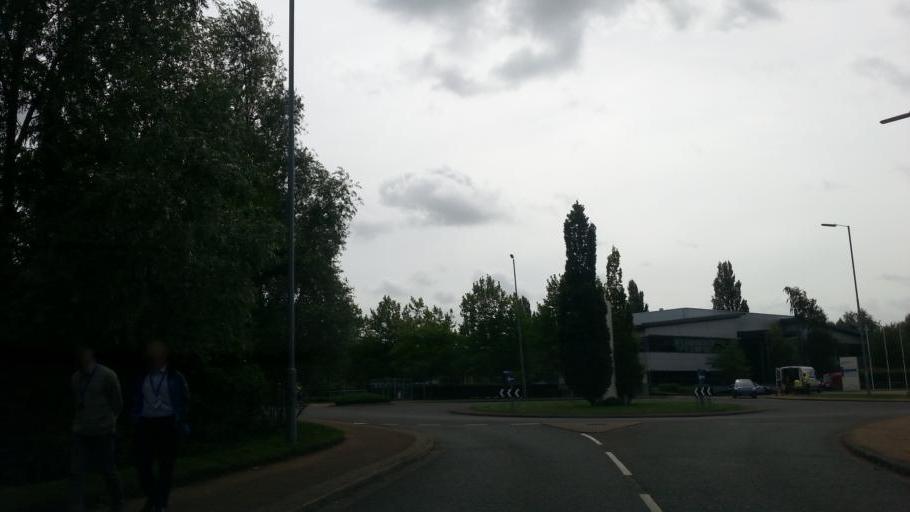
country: GB
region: England
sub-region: Cambridgeshire
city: Waterbeach
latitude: 52.2905
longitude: 0.1733
